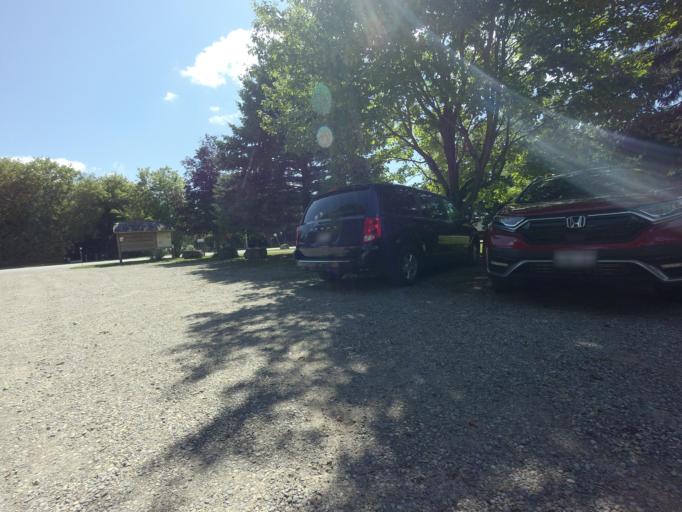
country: CA
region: Ontario
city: Orangeville
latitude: 43.7836
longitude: -80.2269
